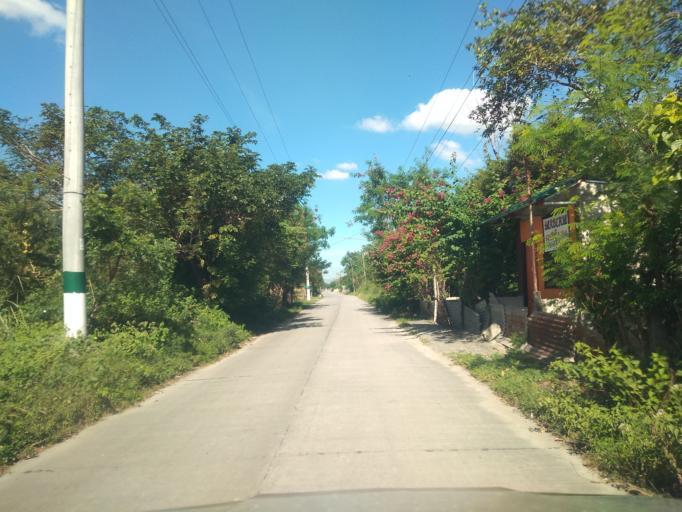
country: PH
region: Central Luzon
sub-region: Province of Pampanga
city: Bacolor
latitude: 15.0098
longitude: 120.6374
